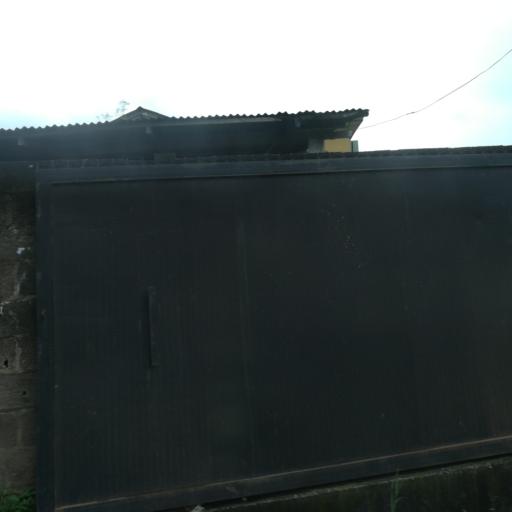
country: NG
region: Lagos
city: Agege
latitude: 6.6075
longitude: 3.3014
